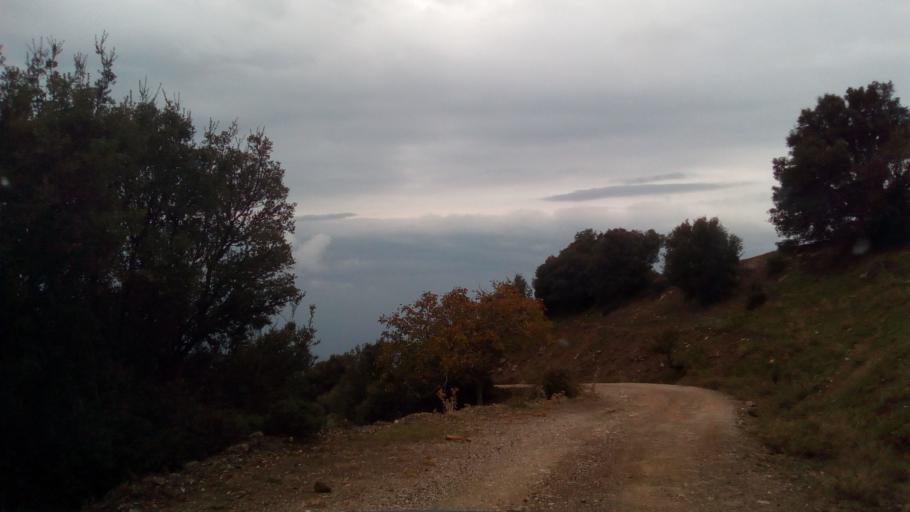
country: GR
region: West Greece
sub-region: Nomos Achaias
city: Selianitika
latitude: 38.4132
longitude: 22.0891
